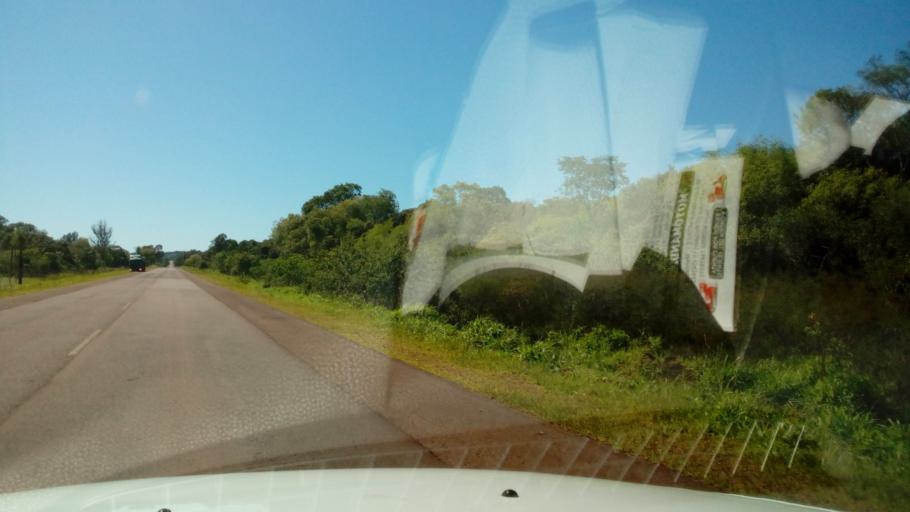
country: AR
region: Misiones
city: Almafuerte
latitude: -27.5700
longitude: -55.3943
